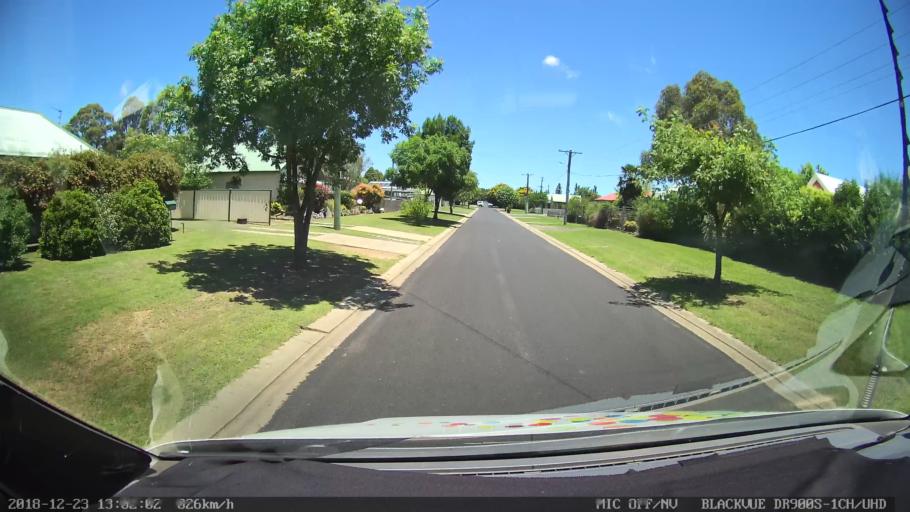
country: AU
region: New South Wales
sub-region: Armidale Dumaresq
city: Armidale
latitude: -30.5072
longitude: 151.6482
